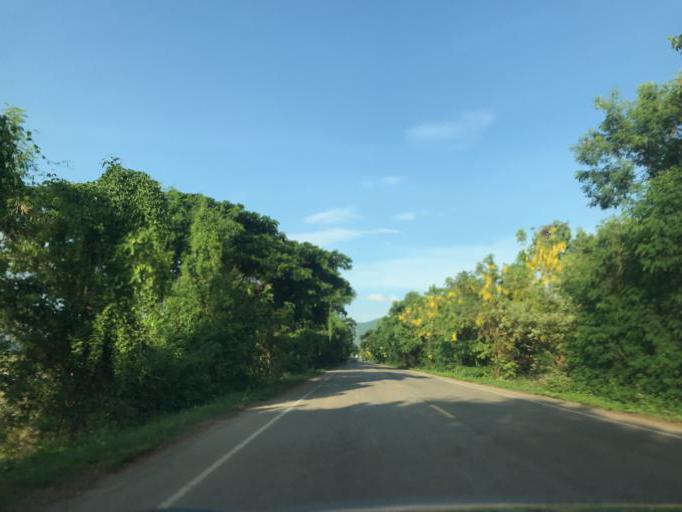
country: TH
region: Phayao
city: Phu Kam Yao
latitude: 19.3130
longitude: 100.0092
